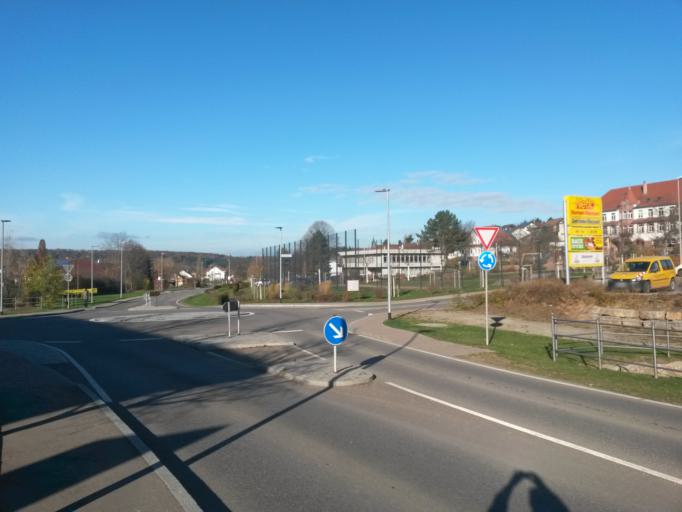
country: DE
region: Baden-Wuerttemberg
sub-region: Karlsruhe Region
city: Neuenburg
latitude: 48.8703
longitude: 8.5891
